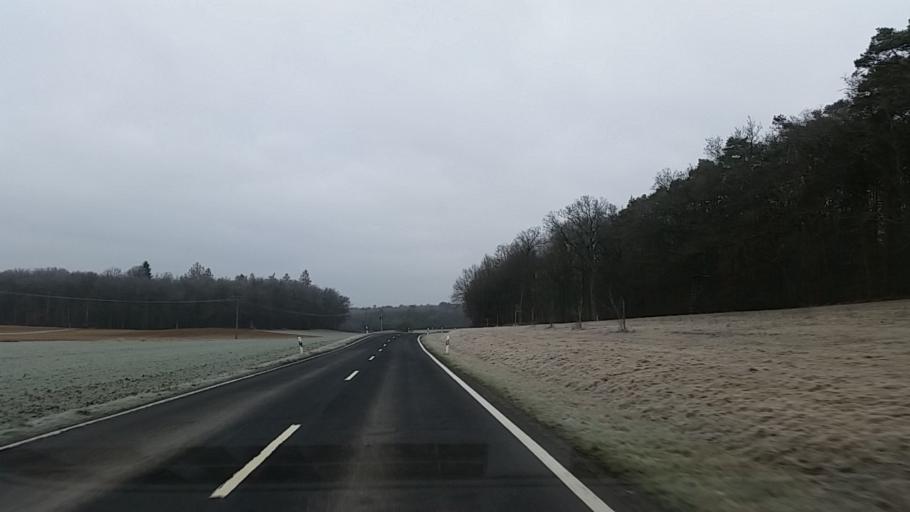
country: DE
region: Bavaria
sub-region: Regierungsbezirk Unterfranken
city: Fuchsstadt
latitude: 50.0695
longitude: 9.9165
